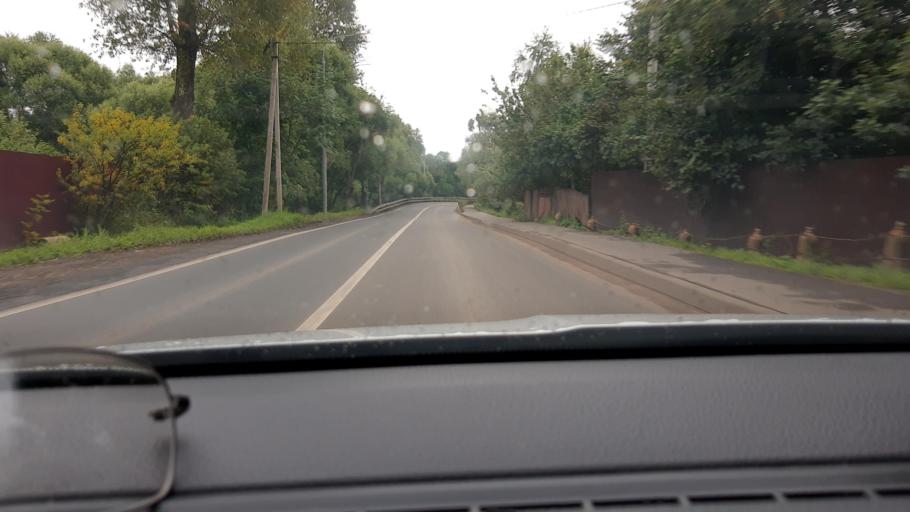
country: RU
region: Moscow
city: Vnukovo
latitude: 55.5975
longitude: 37.2051
